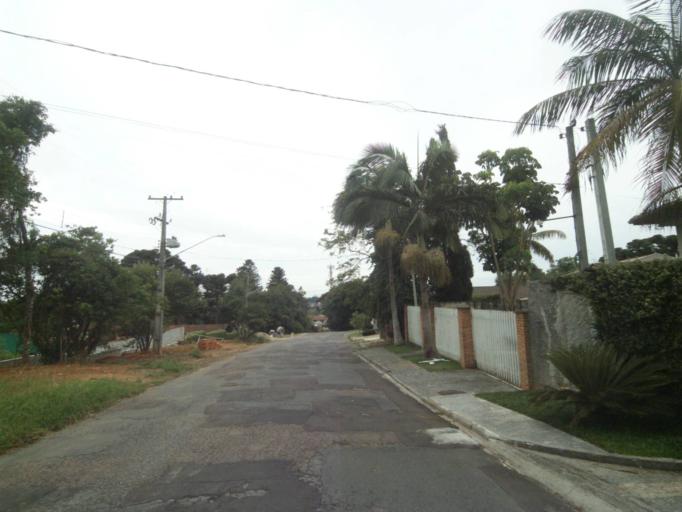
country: BR
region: Parana
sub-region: Curitiba
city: Curitiba
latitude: -25.3937
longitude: -49.2772
